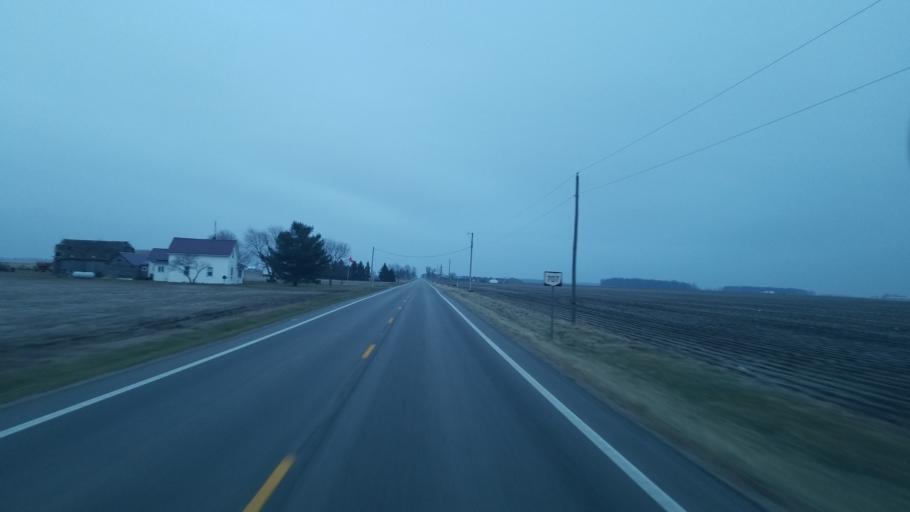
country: US
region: Ohio
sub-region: Mercer County
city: Rockford
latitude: 40.6549
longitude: -84.6885
